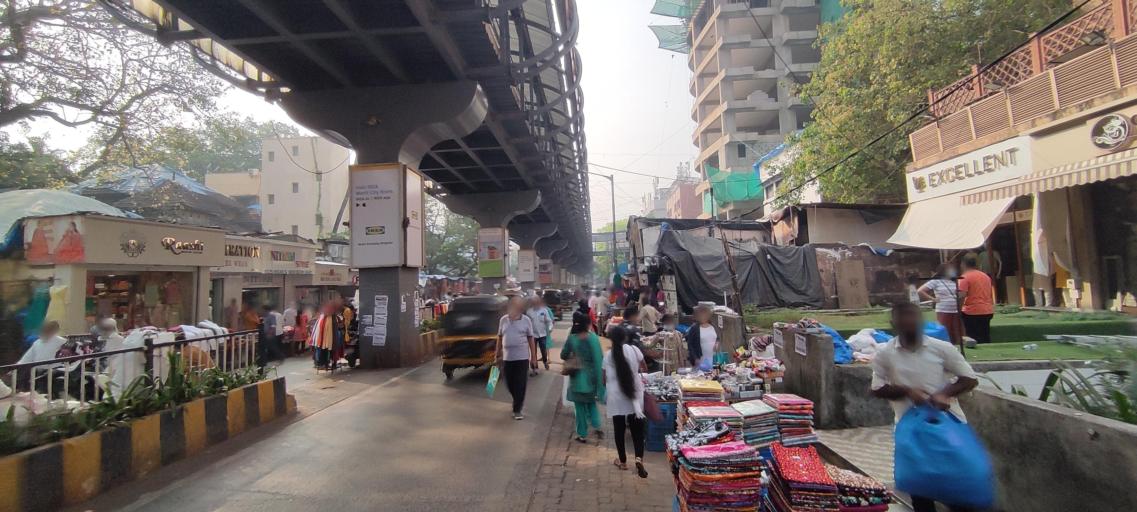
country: IN
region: Maharashtra
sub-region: Mumbai Suburban
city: Mumbai
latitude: 19.0807
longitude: 72.8402
